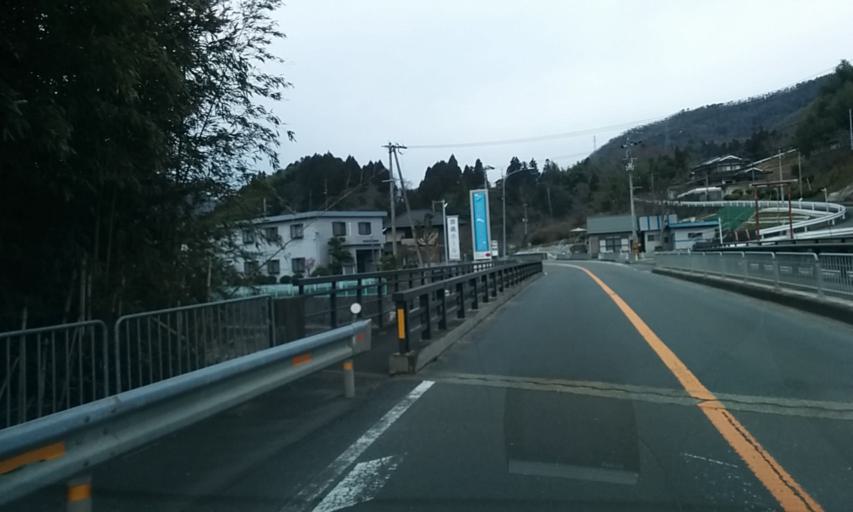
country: JP
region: Kyoto
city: Ayabe
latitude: 35.2124
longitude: 135.4251
